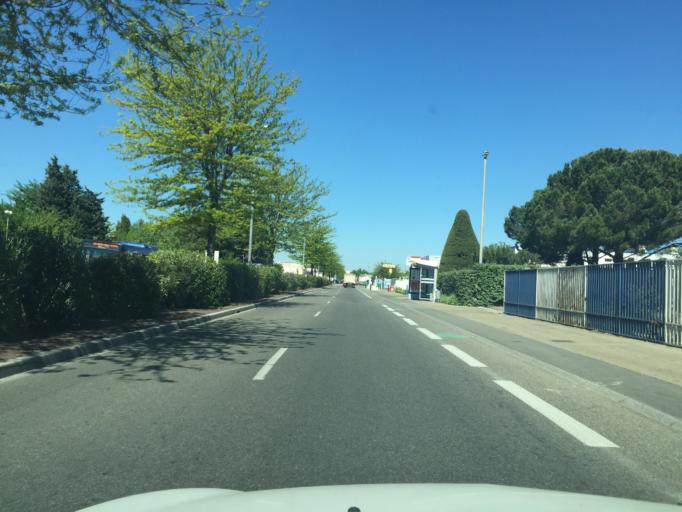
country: FR
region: Provence-Alpes-Cote d'Azur
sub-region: Departement du Vaucluse
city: Le Pontet
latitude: 43.9370
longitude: 4.8446
